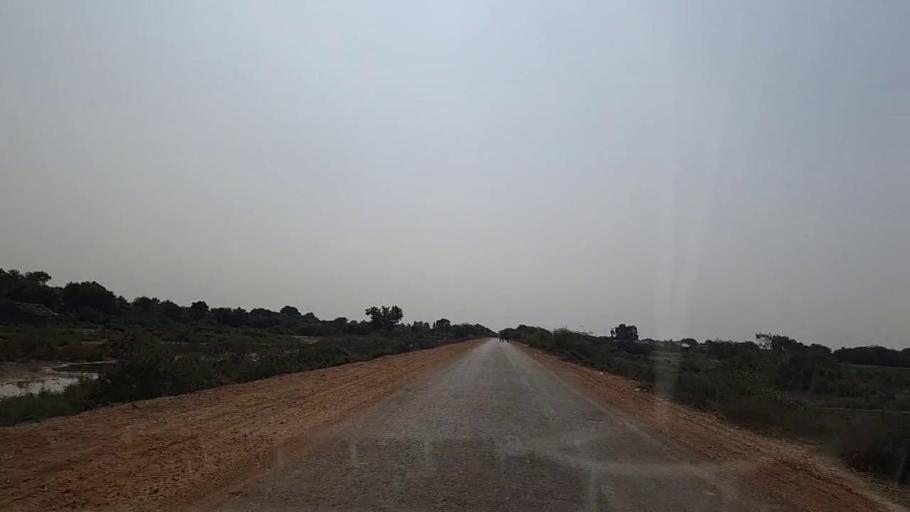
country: PK
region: Sindh
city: Chuhar Jamali
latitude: 24.2572
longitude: 67.9073
